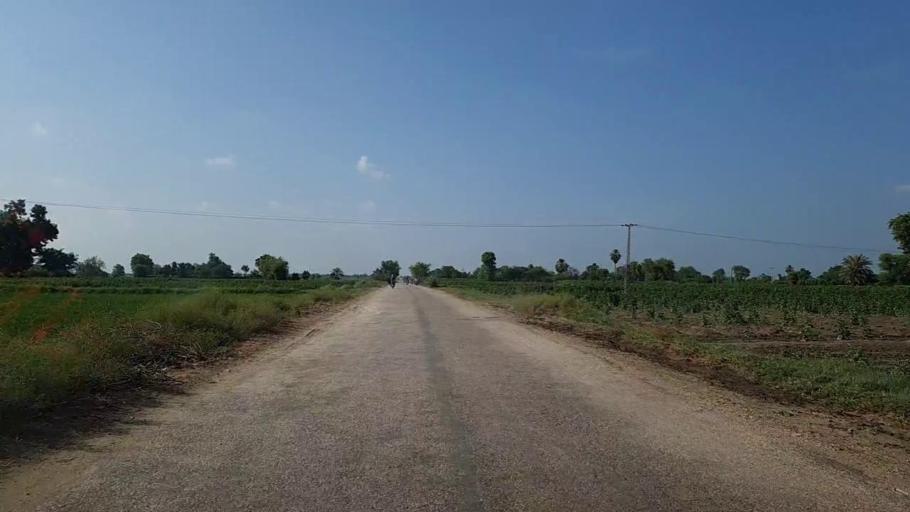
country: PK
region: Sindh
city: Kandiaro
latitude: 27.0571
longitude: 68.3171
